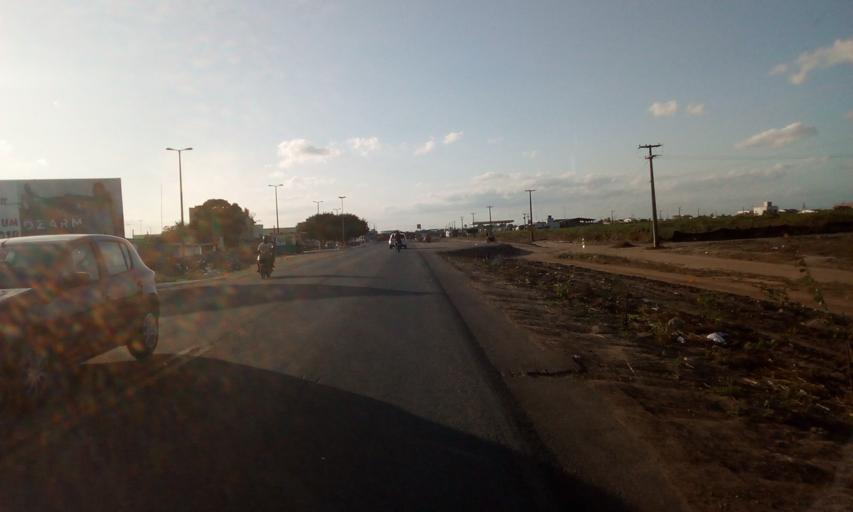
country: BR
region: Paraiba
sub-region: Mari
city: Mari
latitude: -7.0565
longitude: -35.3118
